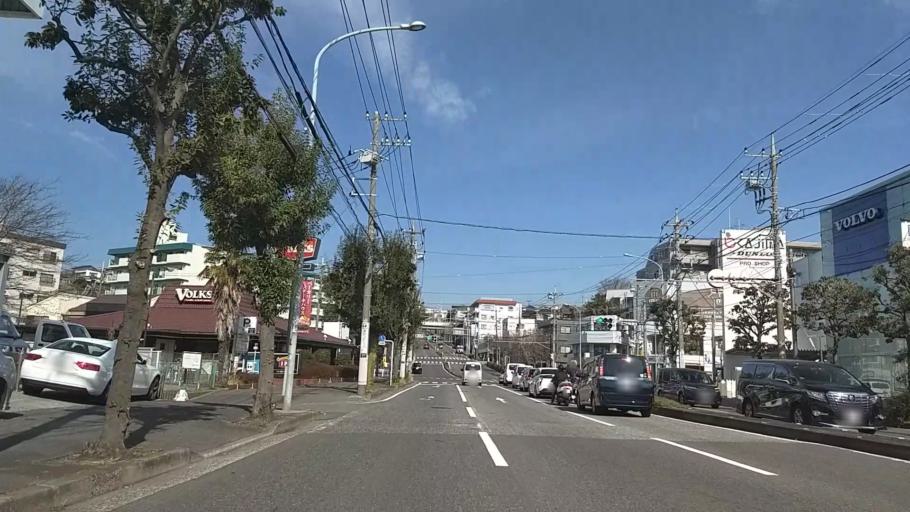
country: JP
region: Kanagawa
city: Kamakura
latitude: 35.3822
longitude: 139.5776
